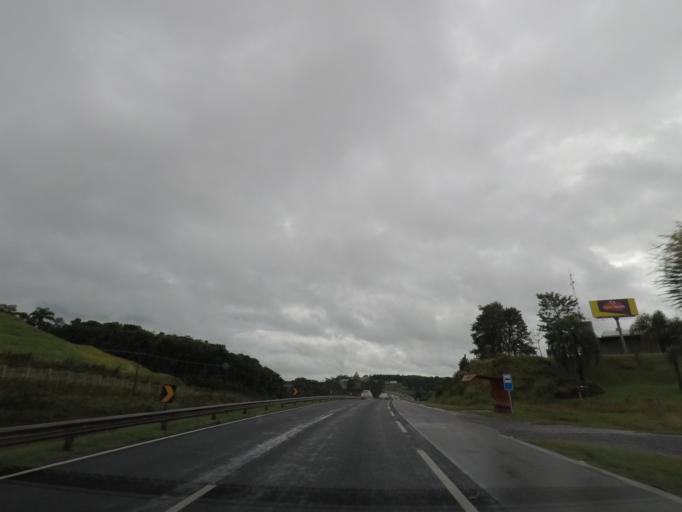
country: BR
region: Parana
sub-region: Campo Largo
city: Campo Largo
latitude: -25.4314
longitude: -49.4208
